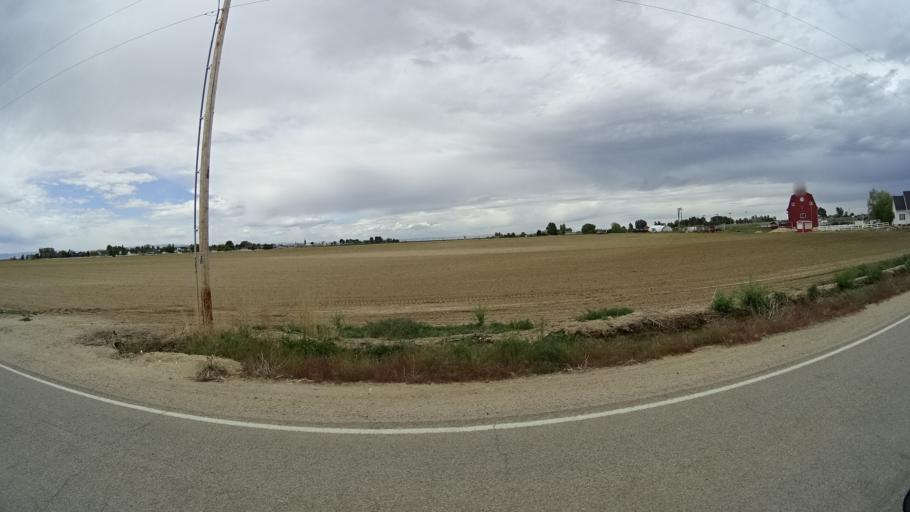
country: US
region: Idaho
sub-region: Ada County
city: Kuna
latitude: 43.5384
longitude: -116.4138
